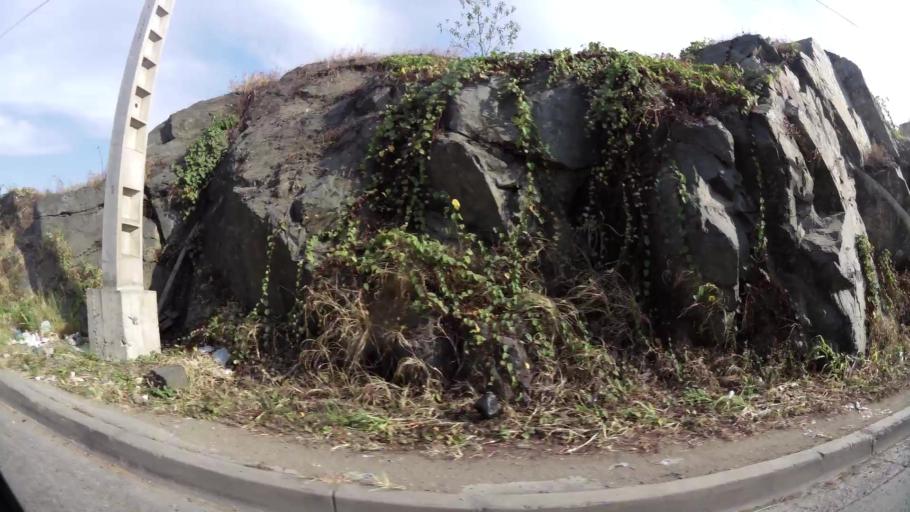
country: EC
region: Guayas
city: Eloy Alfaro
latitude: -2.0717
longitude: -79.9168
